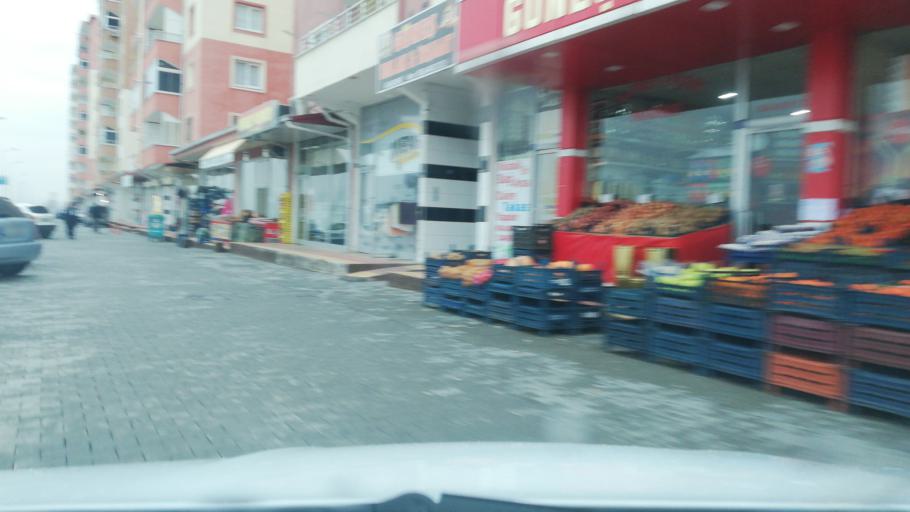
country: TR
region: Kahramanmaras
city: Kahramanmaras
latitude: 37.5796
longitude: 36.9999
